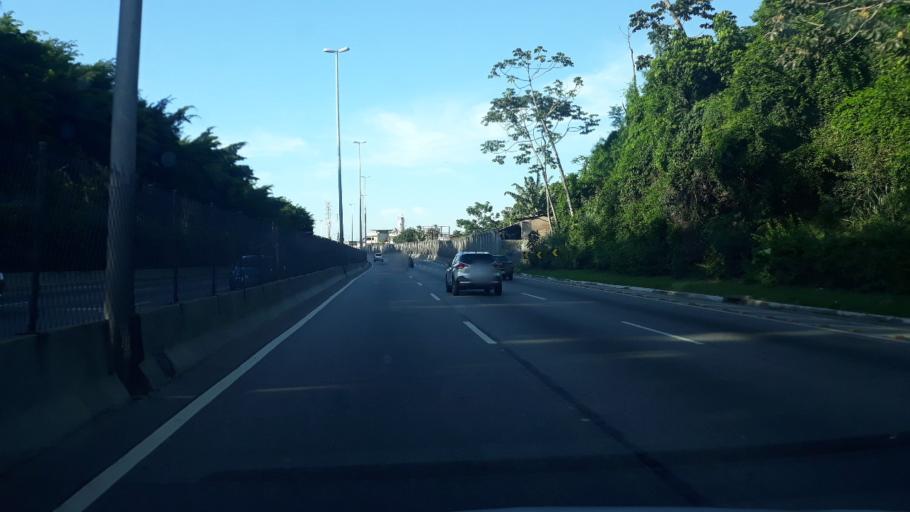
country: BR
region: Rio de Janeiro
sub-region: Sao Joao De Meriti
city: Sao Joao de Meriti
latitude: -22.9478
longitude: -43.3555
